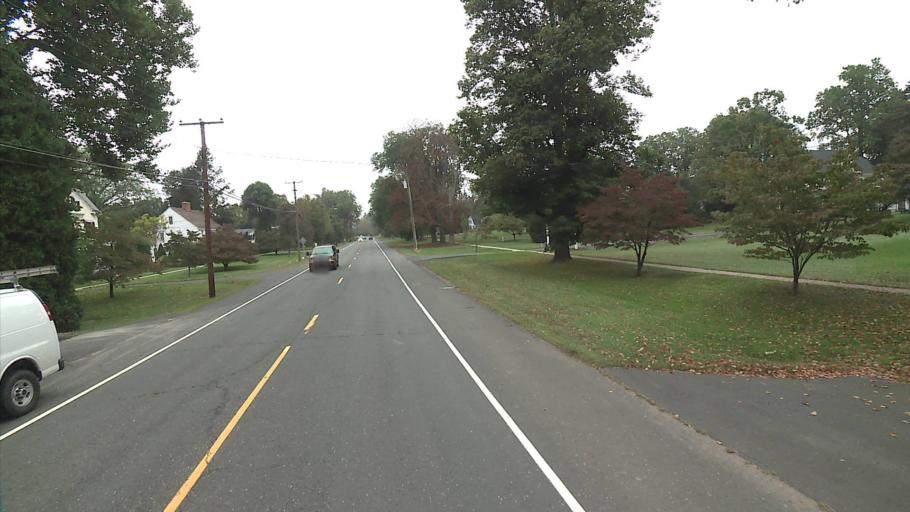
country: US
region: Connecticut
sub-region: Hartford County
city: Suffield Depot
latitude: 41.9886
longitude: -72.6485
